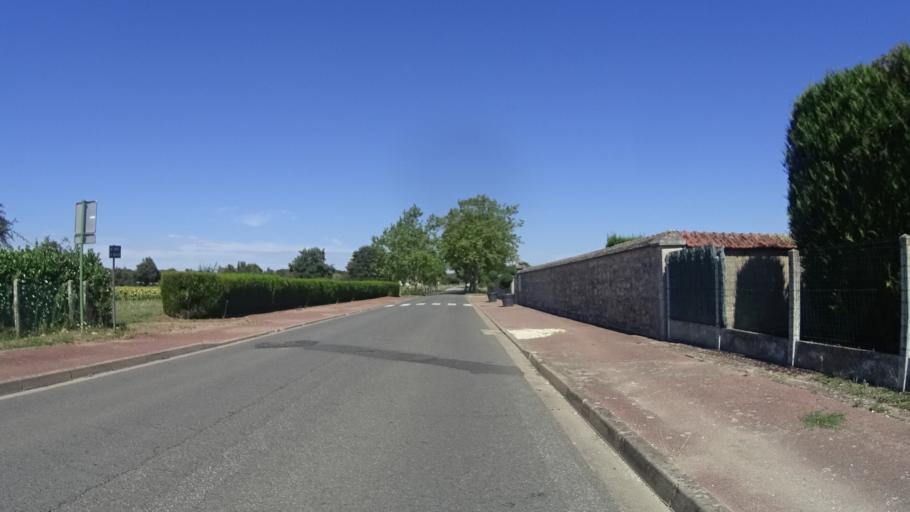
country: FR
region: Centre
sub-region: Departement du Cher
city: Belleville-sur-Loire
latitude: 47.5120
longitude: 2.8473
